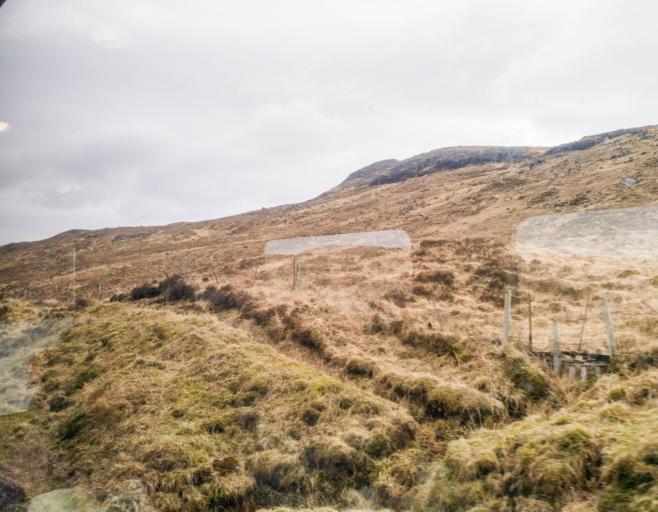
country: GB
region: Scotland
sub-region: Highland
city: Spean Bridge
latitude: 56.5902
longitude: -4.6513
